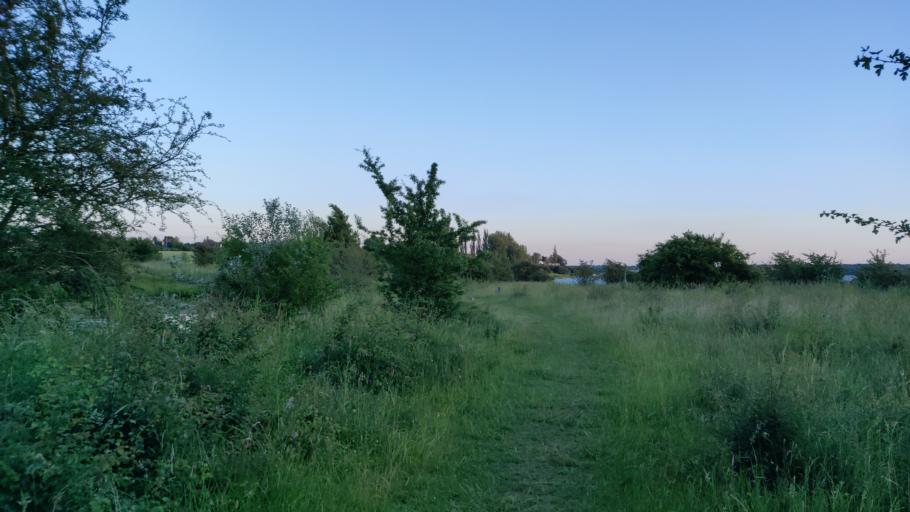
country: DK
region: Zealand
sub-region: Roskilde Kommune
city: Roskilde
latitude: 55.6858
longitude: 12.0765
